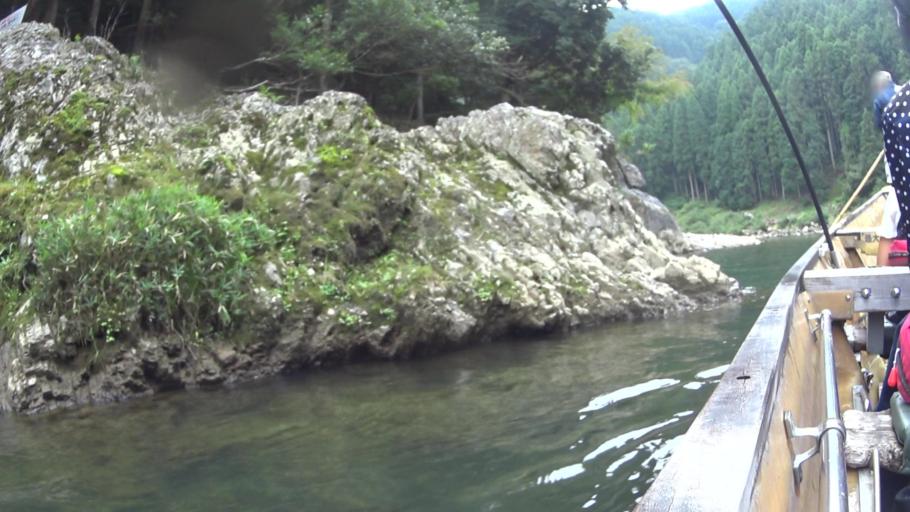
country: JP
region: Kyoto
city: Kameoka
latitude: 35.0189
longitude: 135.6316
